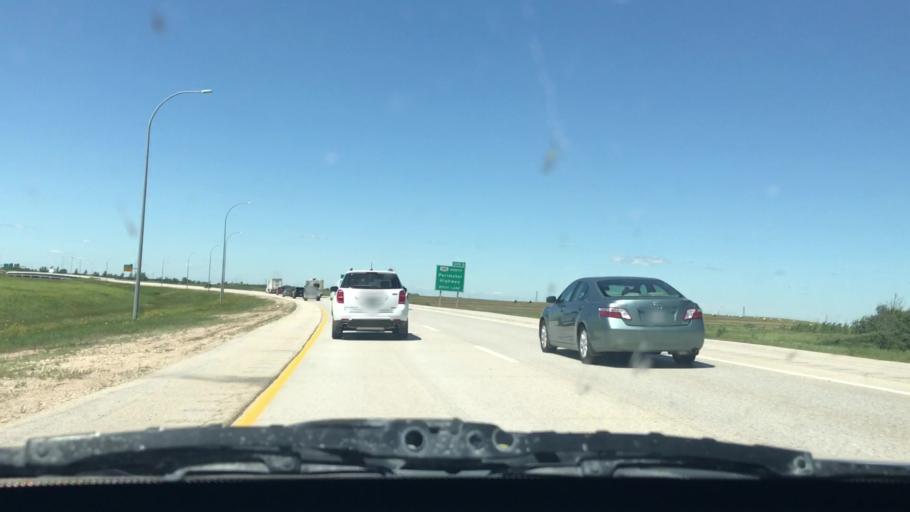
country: CA
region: Manitoba
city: Winnipeg
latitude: 49.8270
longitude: -96.9474
